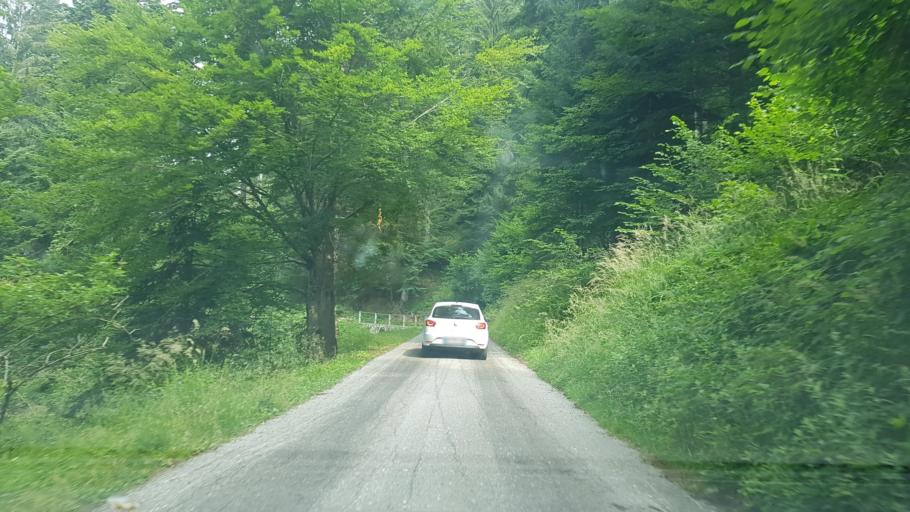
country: IT
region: Friuli Venezia Giulia
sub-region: Provincia di Udine
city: Paularo
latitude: 46.5625
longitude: 13.1196
